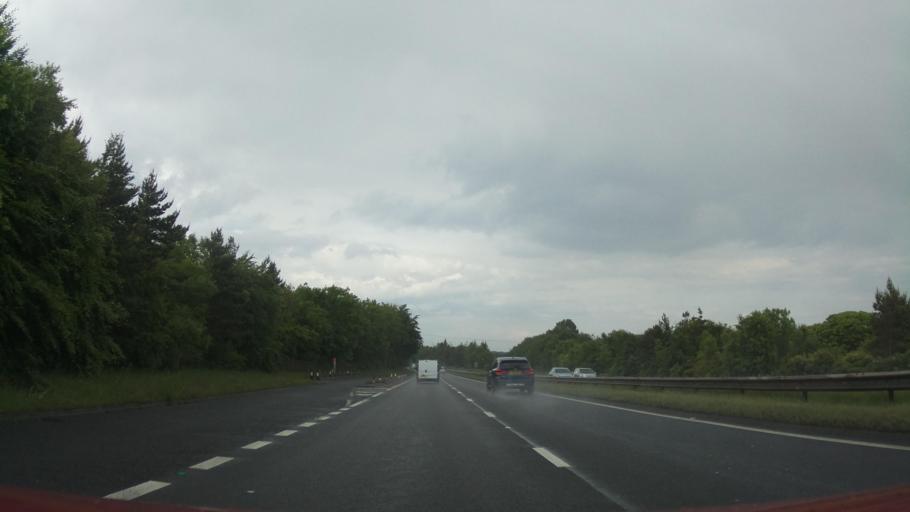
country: GB
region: England
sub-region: County Durham
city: Seaham
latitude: 54.8396
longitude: -1.3762
